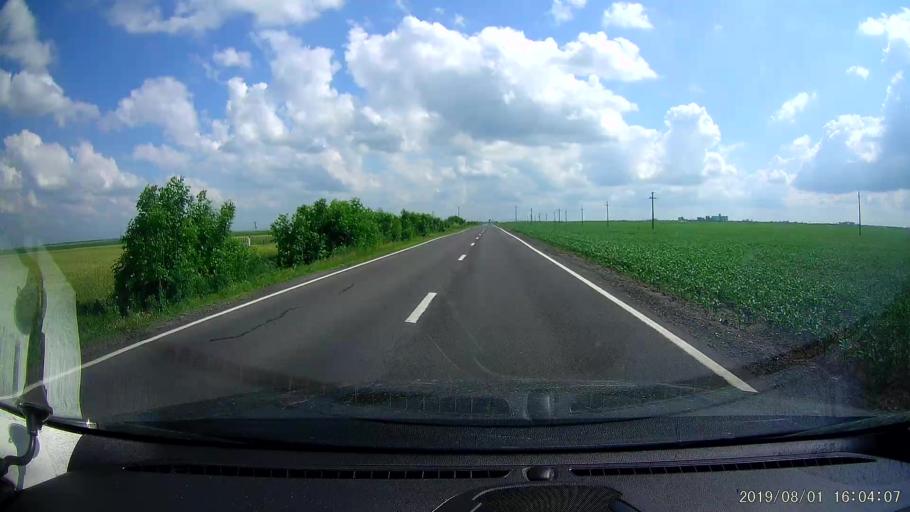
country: RO
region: Calarasi
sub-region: Comuna Dragalina
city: Drajna Noua
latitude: 44.4558
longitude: 27.3815
